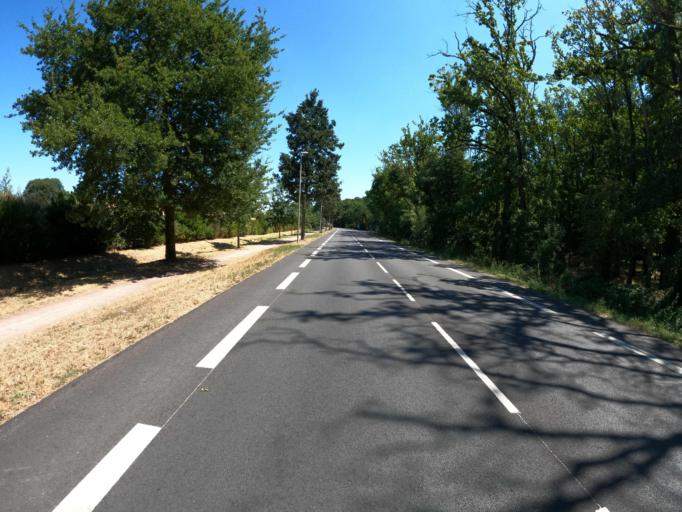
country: FR
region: Pays de la Loire
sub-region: Departement de la Vendee
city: Challans
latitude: 46.8392
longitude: -1.8916
